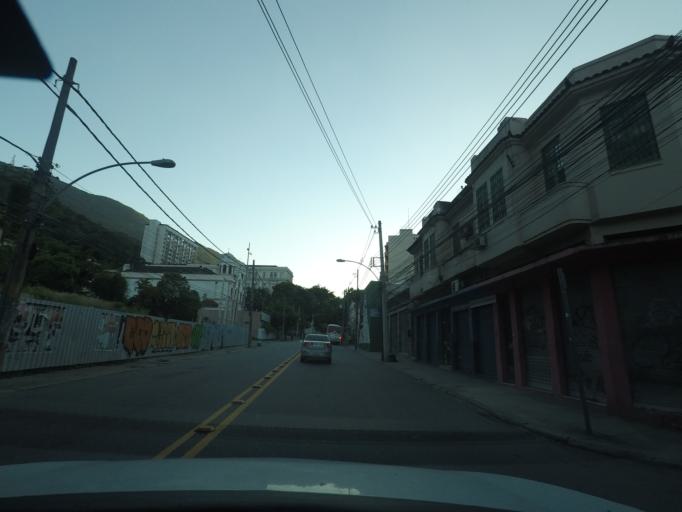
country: BR
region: Rio de Janeiro
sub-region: Rio De Janeiro
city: Rio de Janeiro
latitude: -22.9385
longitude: -43.2472
